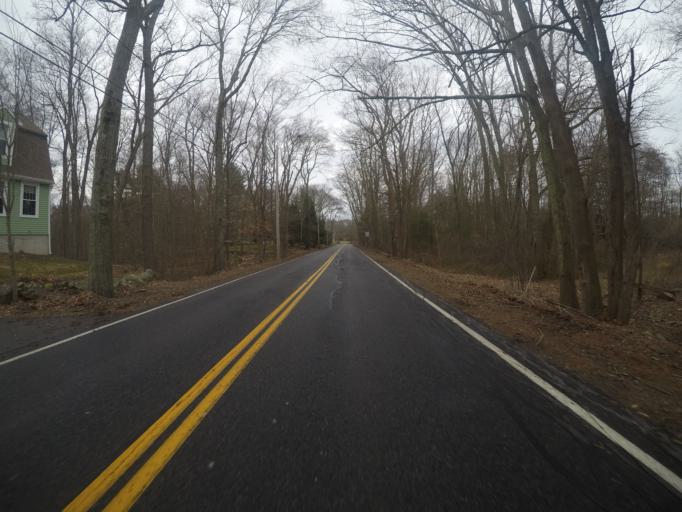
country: US
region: Massachusetts
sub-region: Bristol County
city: Easton
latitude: 42.0411
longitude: -71.1420
